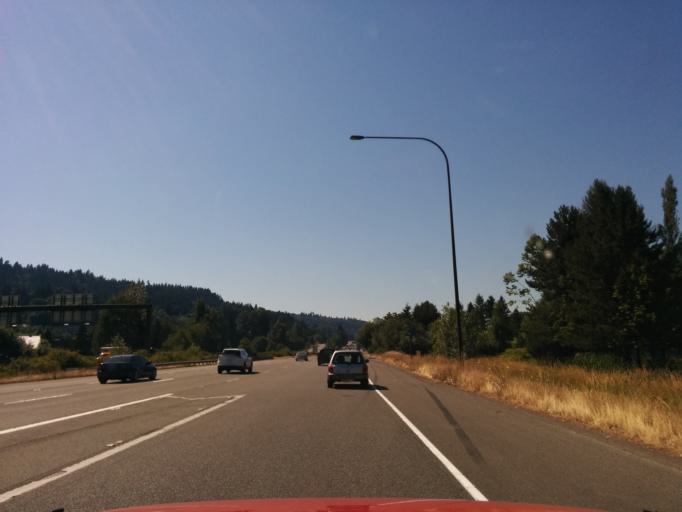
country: US
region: Washington
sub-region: King County
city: Issaquah
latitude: 47.5508
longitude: -122.0663
